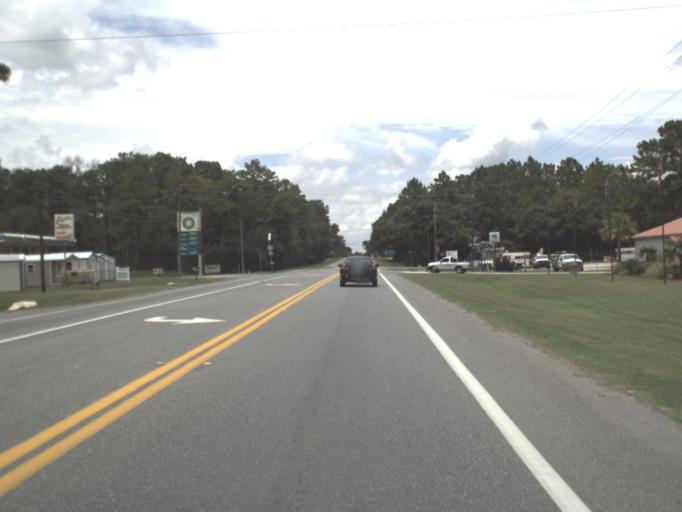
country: US
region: Florida
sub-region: Suwannee County
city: Live Oak
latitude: 30.2667
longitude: -82.9878
